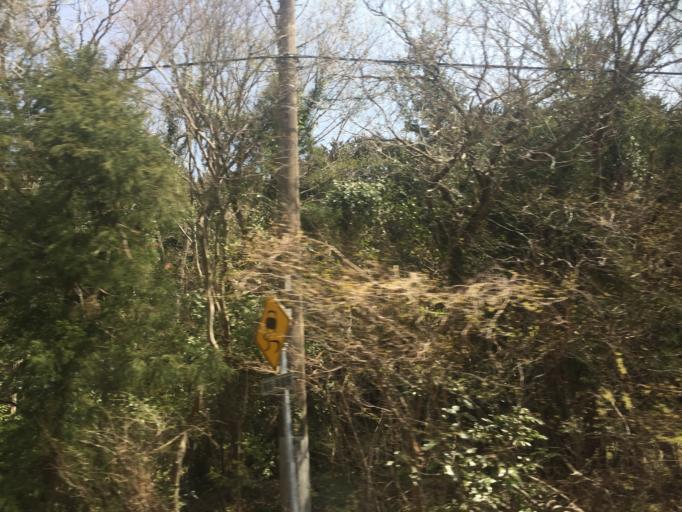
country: JP
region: Shizuoka
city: Ito
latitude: 34.9043
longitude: 139.0887
